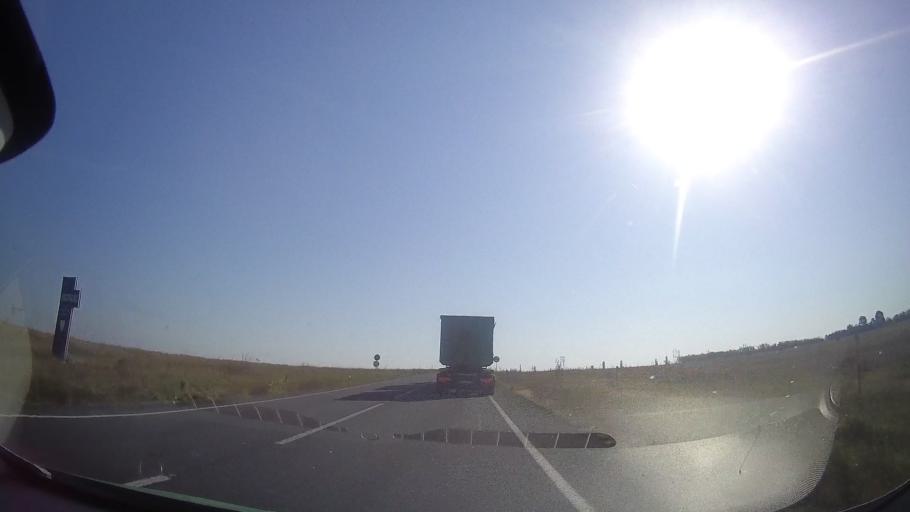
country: RO
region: Timis
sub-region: Comuna Ghizela
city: Ghizela
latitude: 45.7769
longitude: 21.6903
